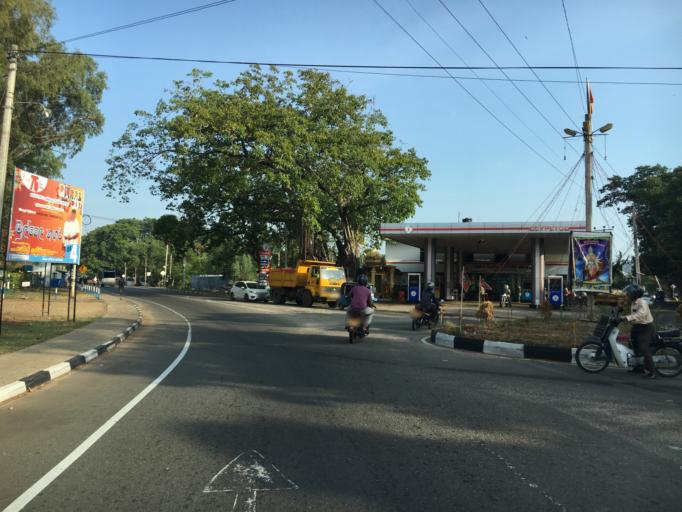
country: LK
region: Eastern Province
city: Eravur Town
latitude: 7.9081
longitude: 81.5338
